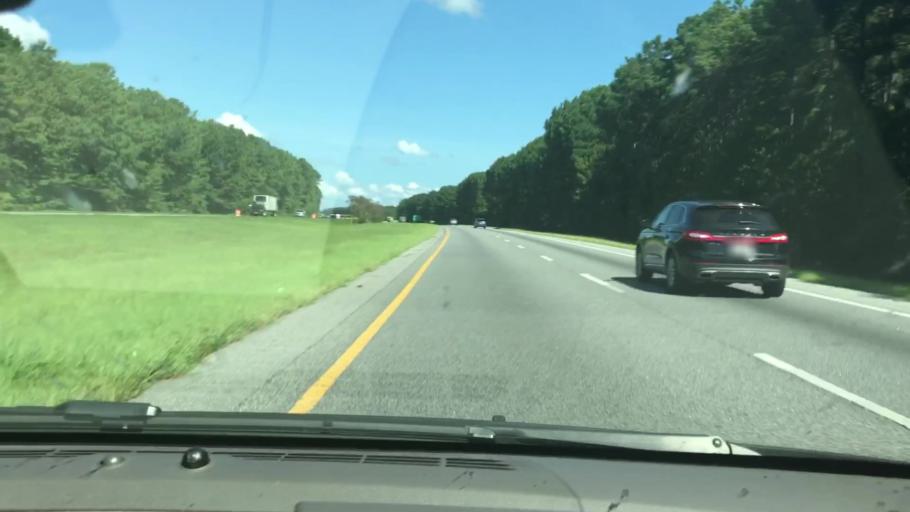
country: US
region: Georgia
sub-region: Harris County
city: Hamilton
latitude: 32.6529
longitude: -84.9735
